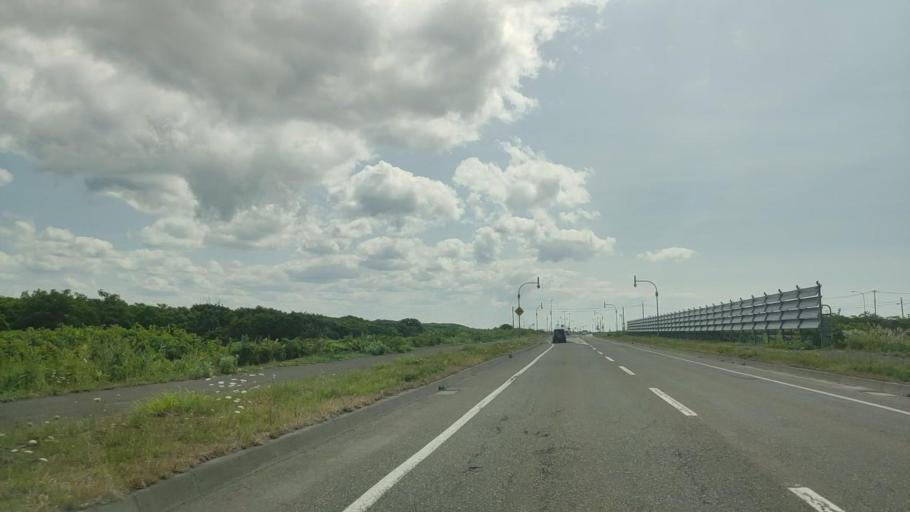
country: JP
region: Hokkaido
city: Makubetsu
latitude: 44.8743
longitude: 141.7513
